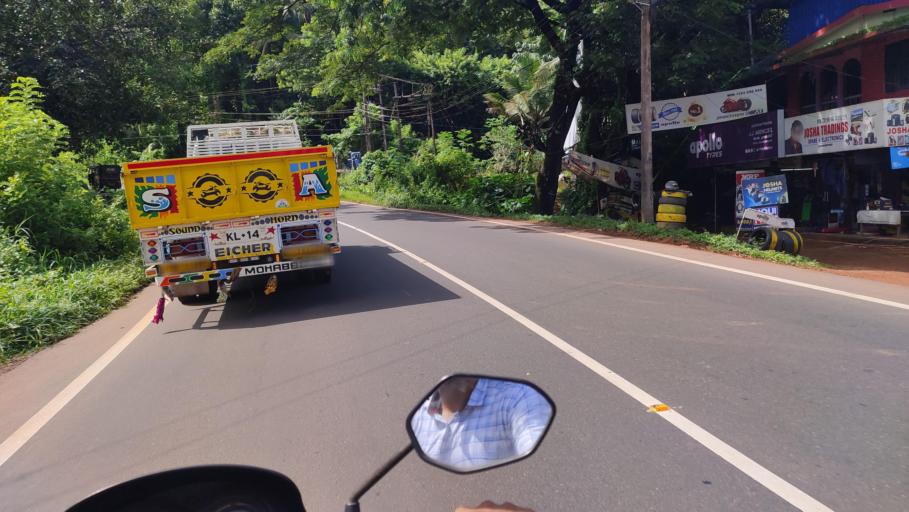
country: IN
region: Kerala
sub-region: Kasaragod District
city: Nileshwar
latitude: 12.2191
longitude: 75.1623
